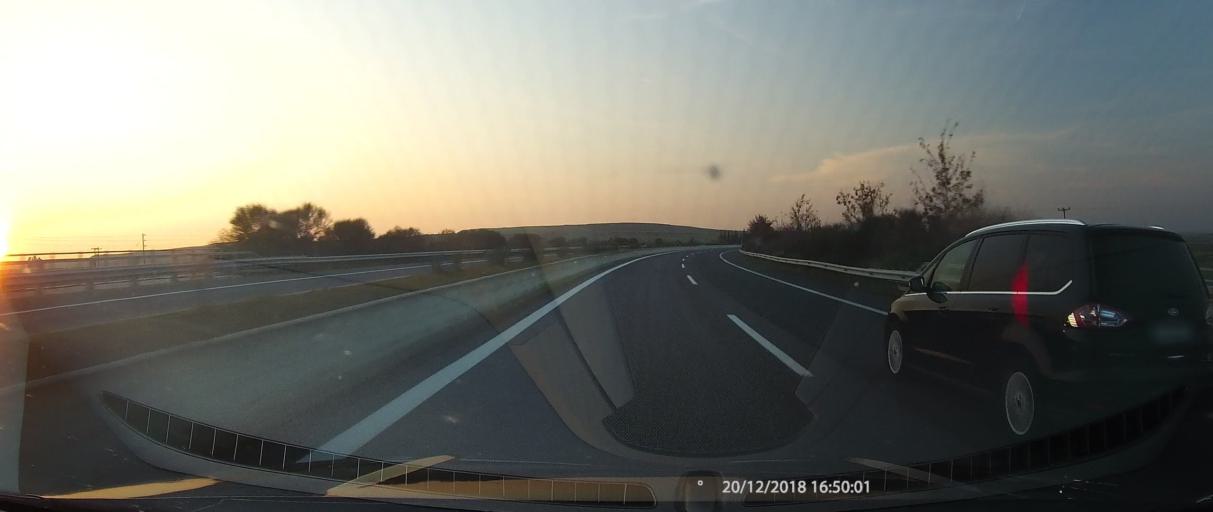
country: GR
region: Thessaly
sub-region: Nomos Larisis
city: Chalki
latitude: 39.4956
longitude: 22.5974
